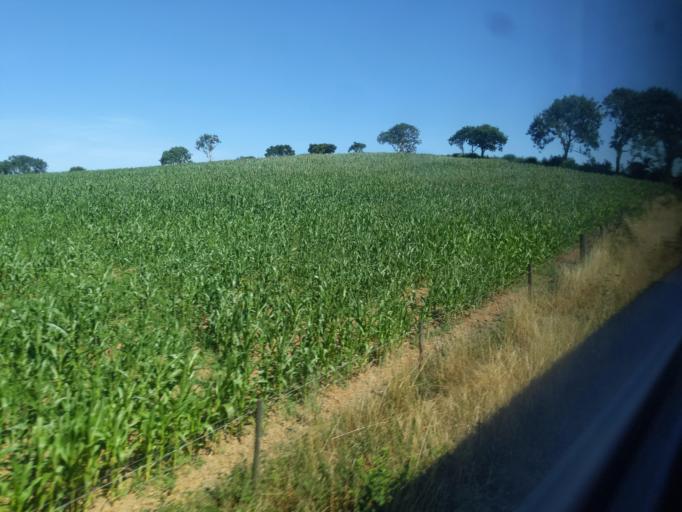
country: GB
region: England
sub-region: Devon
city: Buckfastleigh
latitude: 50.4285
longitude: -3.7674
